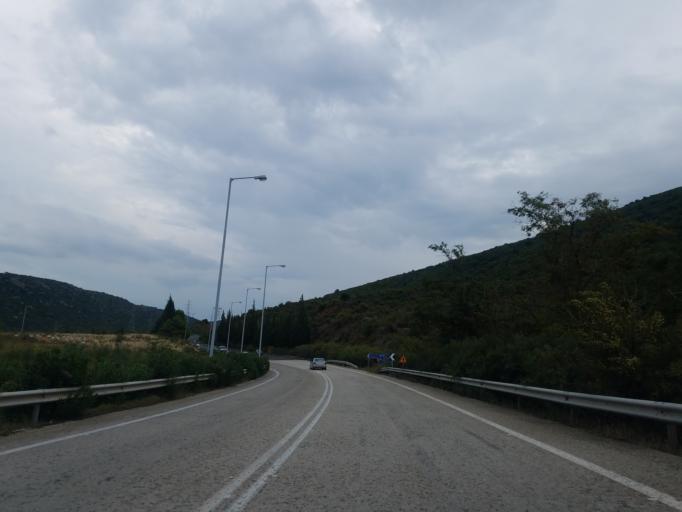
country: GR
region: Central Greece
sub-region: Nomos Voiotias
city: Livadeia
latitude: 38.4475
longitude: 22.7919
